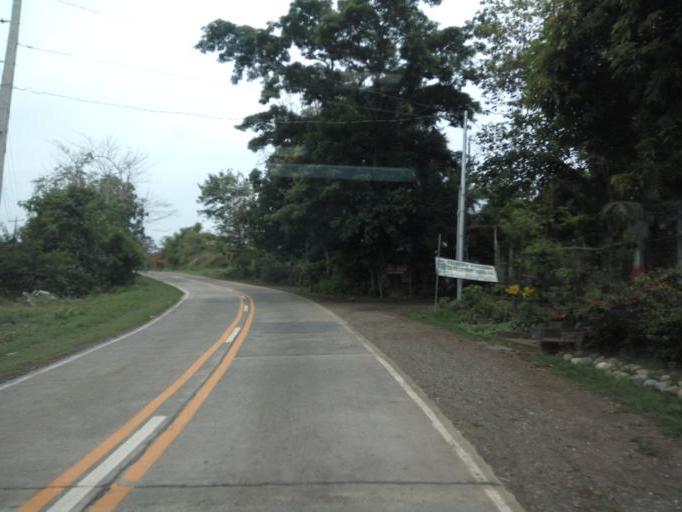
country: PH
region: Cagayan Valley
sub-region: Province of Quirino
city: Saguday
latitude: 16.5299
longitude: 121.5205
